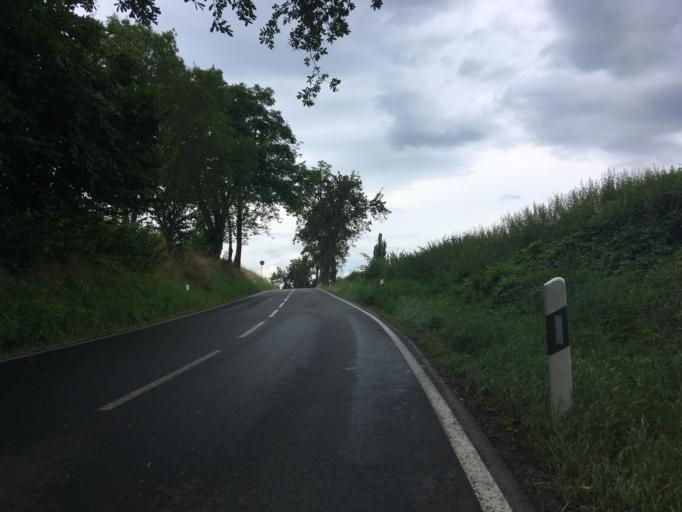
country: DE
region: Saxony
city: Dohma
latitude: 50.9310
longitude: 13.8969
